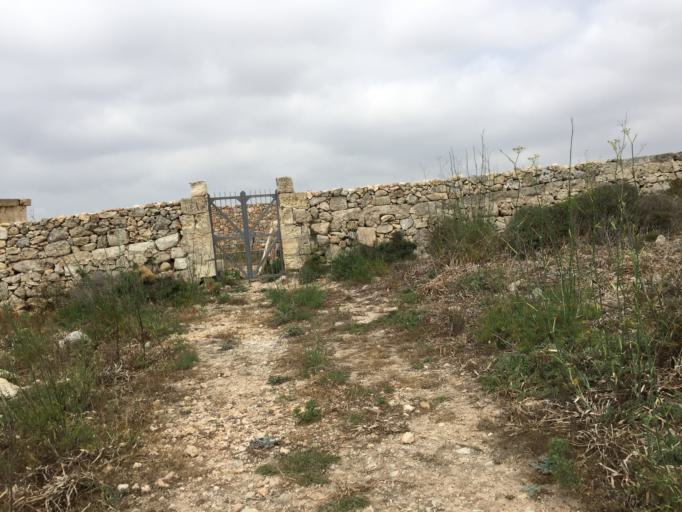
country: MT
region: L-Imgarr
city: Imgarr
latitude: 35.9029
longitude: 14.3467
